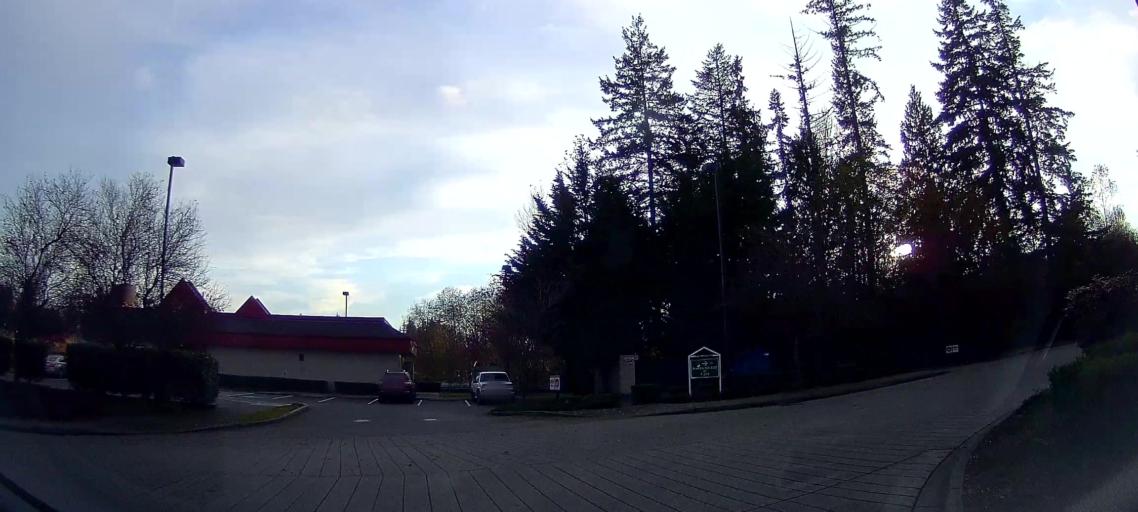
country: US
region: Washington
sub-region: King County
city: Bothell
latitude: 47.7929
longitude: -122.2165
